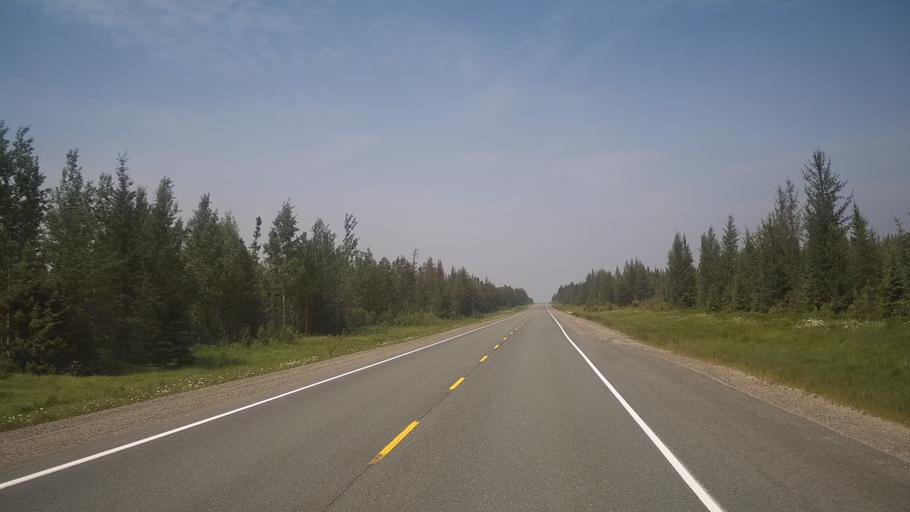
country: CA
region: Ontario
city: Timmins
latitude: 48.7665
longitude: -81.3621
